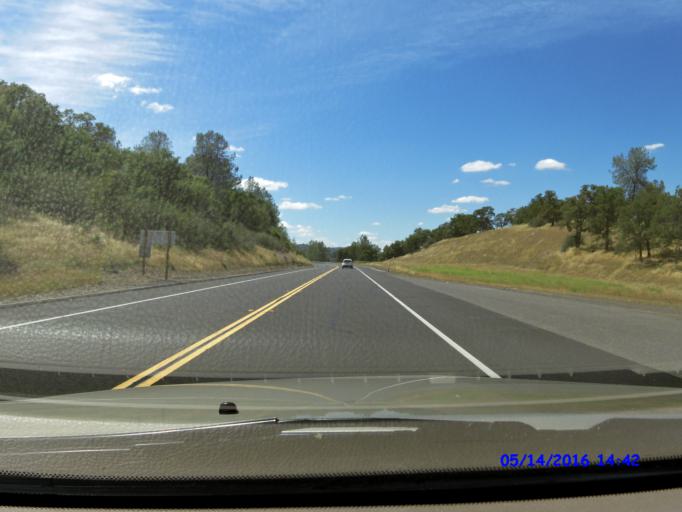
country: US
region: California
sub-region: Tuolumne County
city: Jamestown
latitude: 37.8297
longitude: -120.3460
